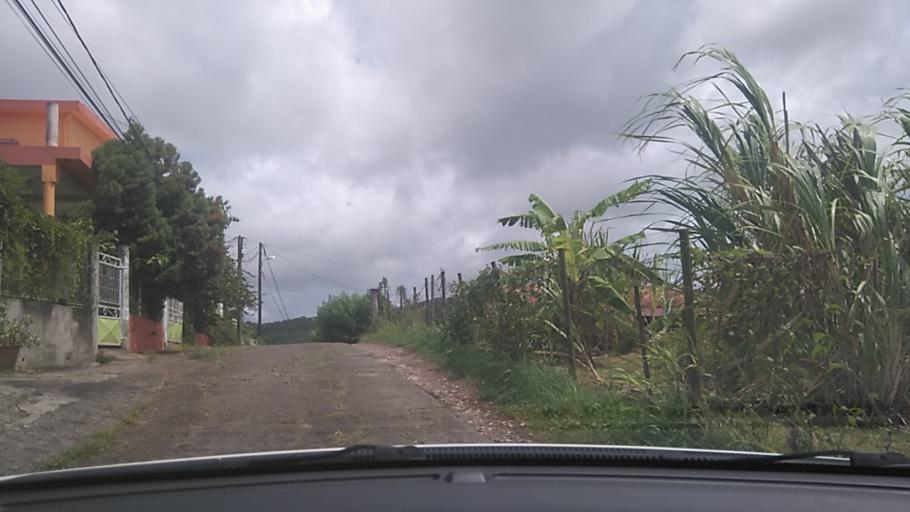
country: MQ
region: Martinique
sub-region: Martinique
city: Saint-Esprit
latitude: 14.5618
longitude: -60.9331
